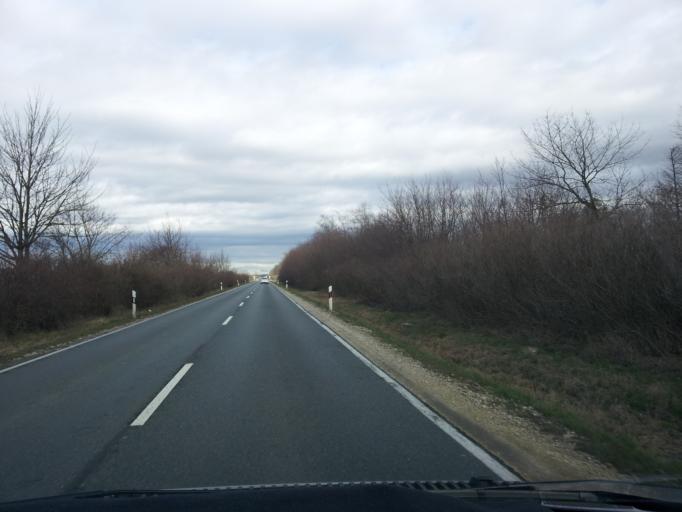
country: HU
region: Vas
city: Gencsapati
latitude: 47.2904
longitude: 16.6095
